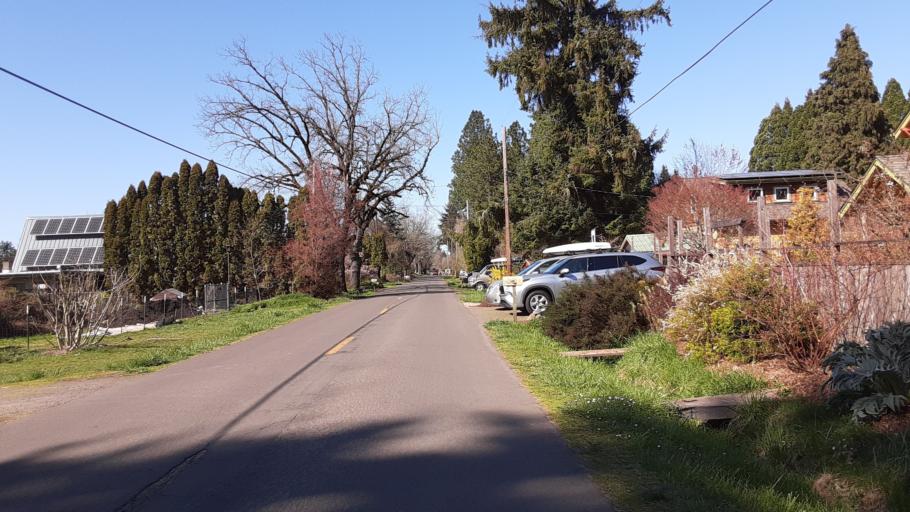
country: US
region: Oregon
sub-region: Benton County
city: Corvallis
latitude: 44.5401
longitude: -123.2556
